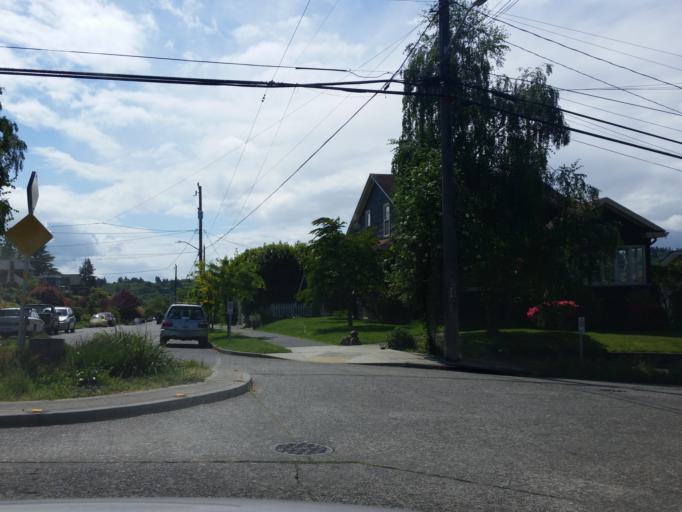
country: US
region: Washington
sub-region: King County
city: Seattle
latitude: 47.6750
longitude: -122.4012
